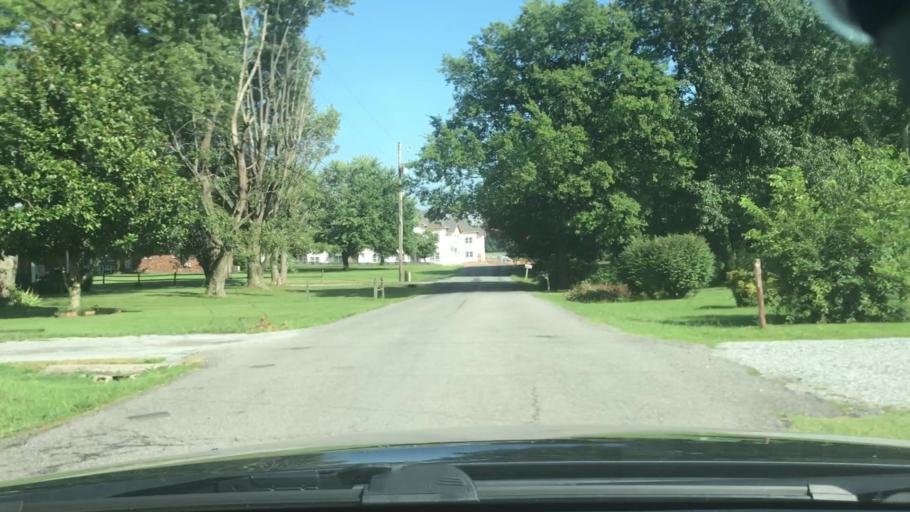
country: US
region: Tennessee
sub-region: Sumner County
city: White House
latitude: 36.4553
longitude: -86.6731
